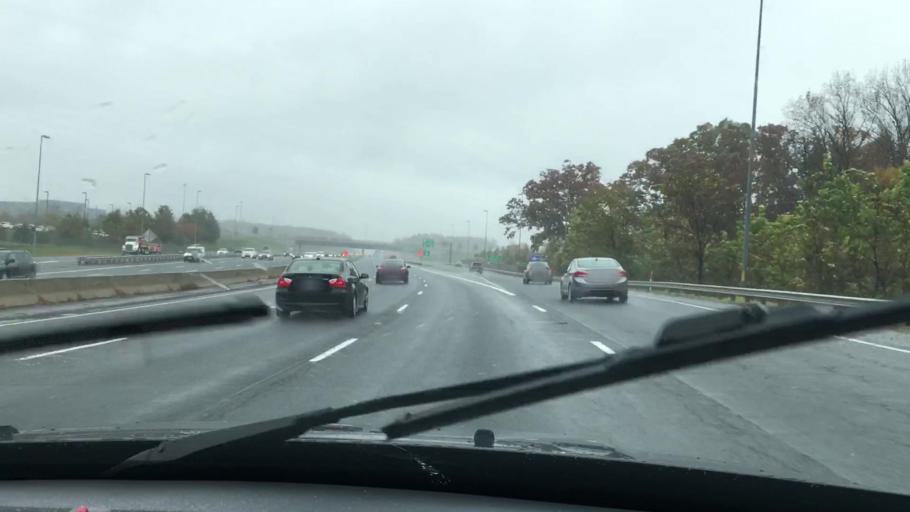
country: US
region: Virginia
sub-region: Fairfax County
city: Chantilly
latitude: 38.8779
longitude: -77.4489
